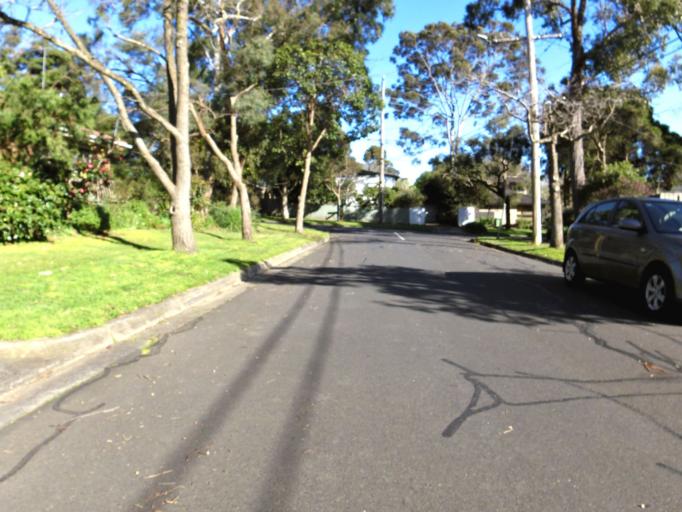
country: AU
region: Victoria
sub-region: Maroondah
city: Heathmont
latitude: -37.8338
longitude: 145.2332
